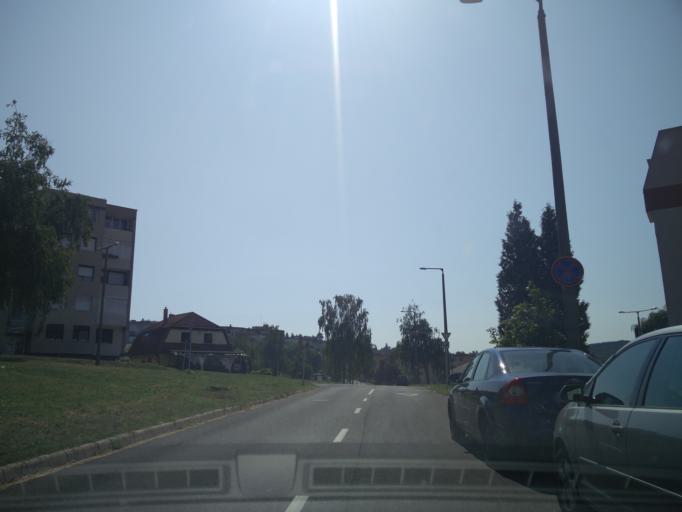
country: HU
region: Zala
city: Zalaegerszeg
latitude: 46.8263
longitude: 16.8295
